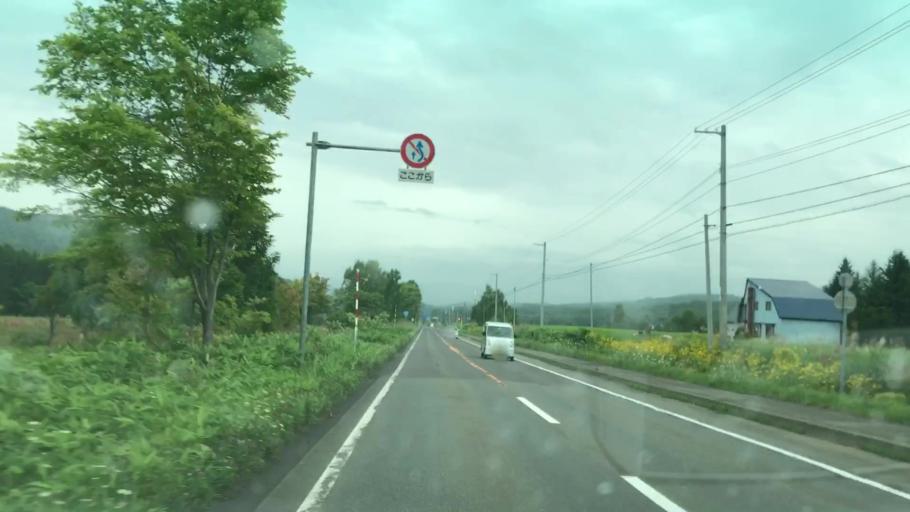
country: JP
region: Hokkaido
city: Niseko Town
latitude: 42.7655
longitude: 140.4828
